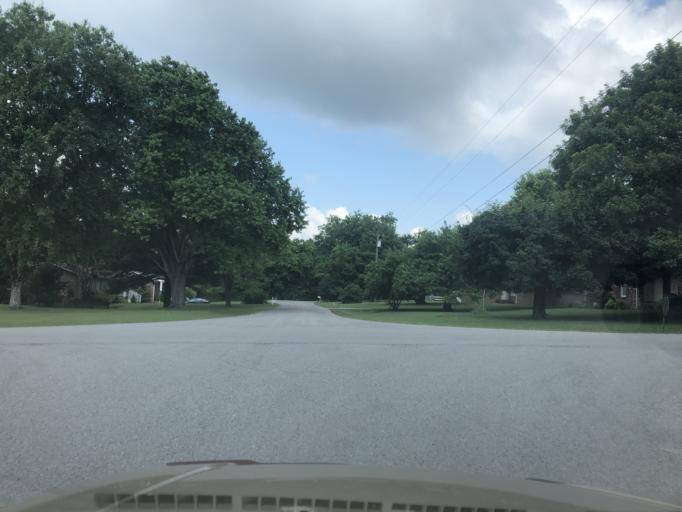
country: US
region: Tennessee
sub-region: Wilson County
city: Green Hill
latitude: 36.2360
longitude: -86.5889
